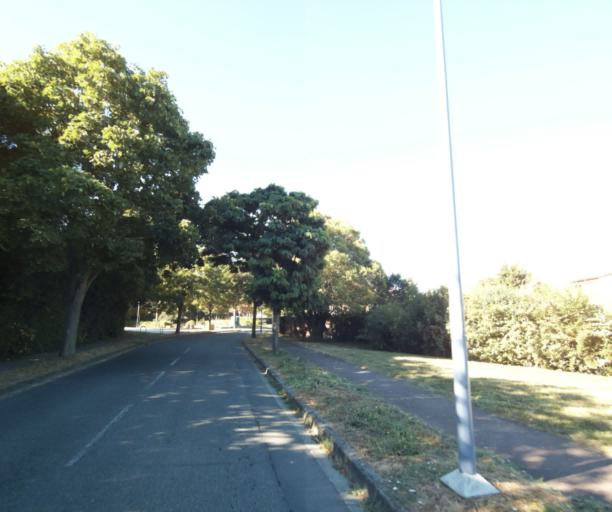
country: FR
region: Midi-Pyrenees
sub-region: Departement de la Haute-Garonne
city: Castanet-Tolosan
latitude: 43.5238
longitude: 1.5077
